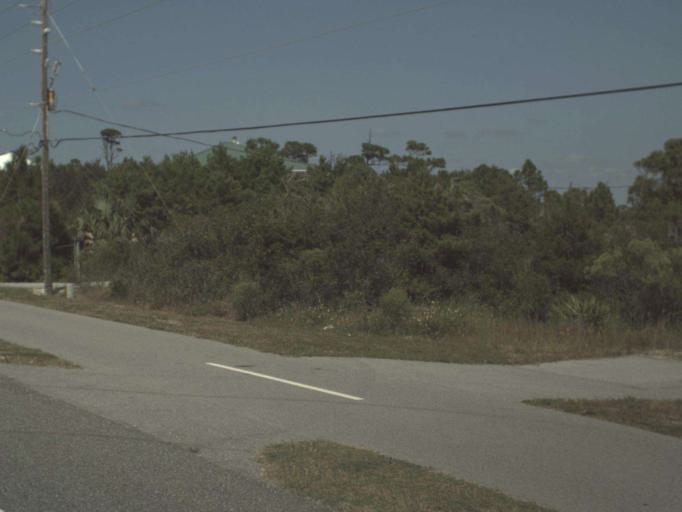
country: US
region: Florida
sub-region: Gulf County
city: Port Saint Joe
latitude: 29.6973
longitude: -85.3754
